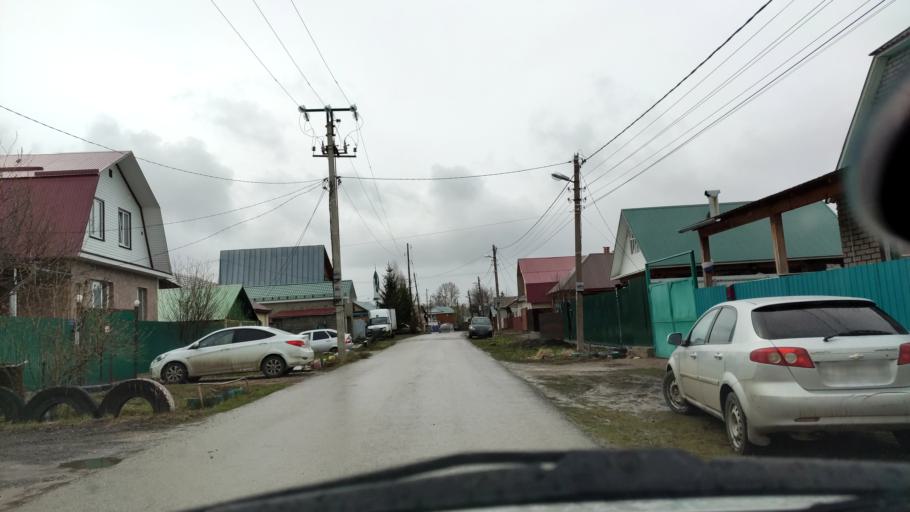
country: RU
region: Bashkortostan
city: Ufa
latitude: 54.7308
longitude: 55.9092
